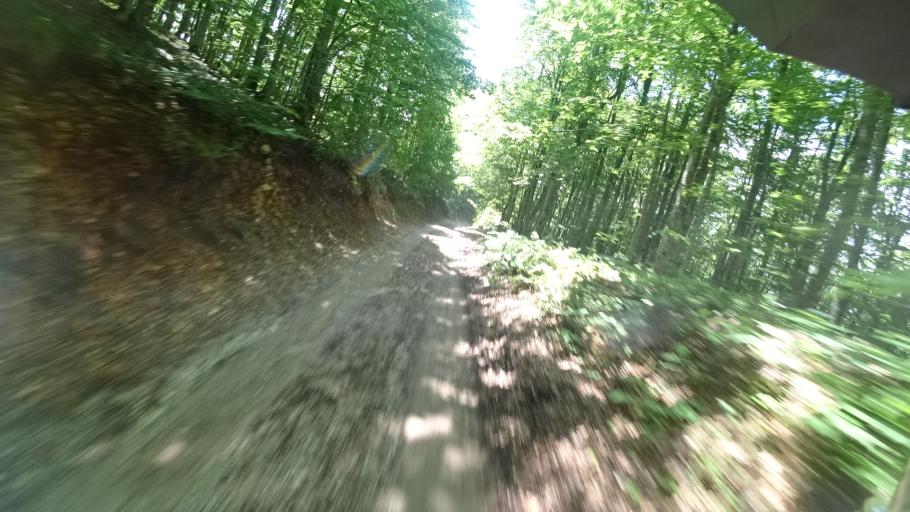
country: BA
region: Federation of Bosnia and Herzegovina
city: Orasac
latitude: 44.5767
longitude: 15.8519
